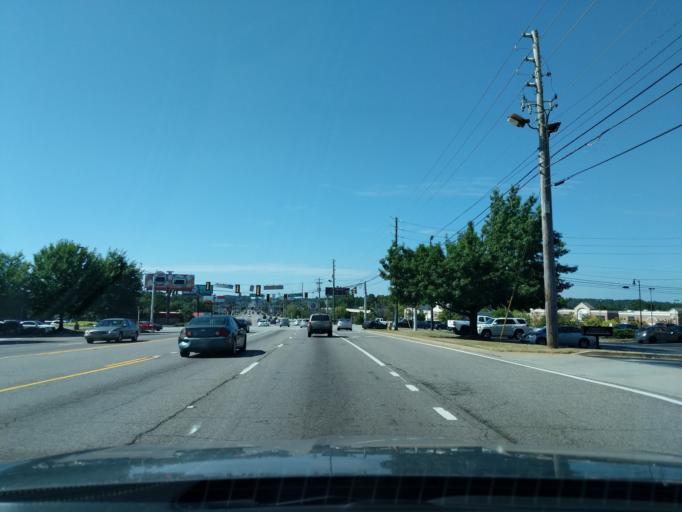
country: US
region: Georgia
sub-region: Columbia County
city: Martinez
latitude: 33.5098
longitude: -82.0272
